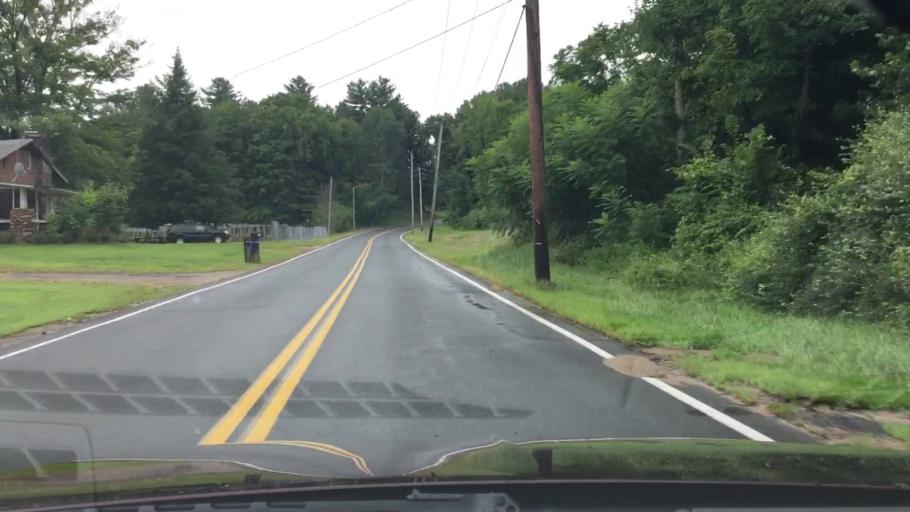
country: US
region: Connecticut
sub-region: Hartford County
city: Tariffville
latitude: 41.9240
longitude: -72.7696
